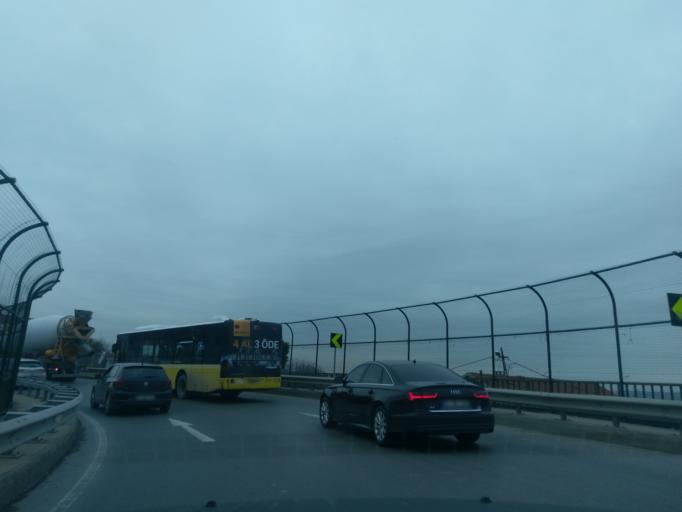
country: TR
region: Istanbul
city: Umraniye
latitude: 41.0997
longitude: 29.0974
